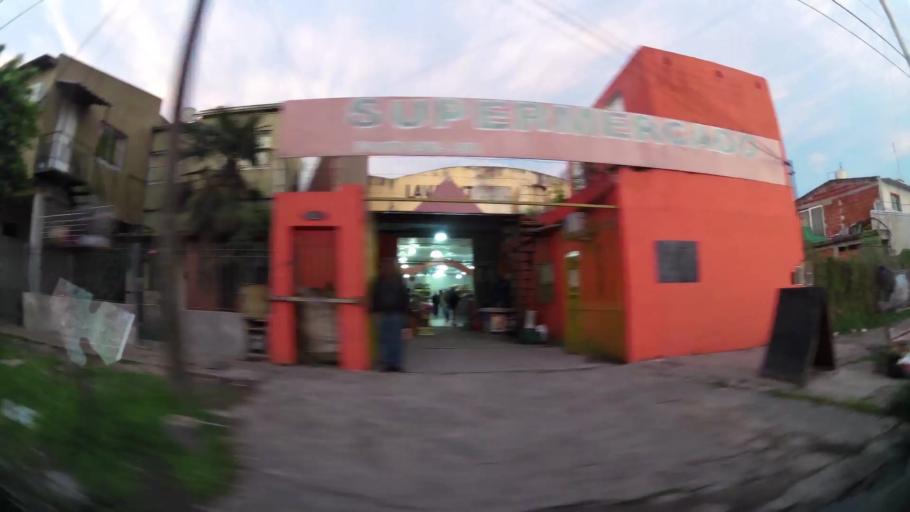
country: AR
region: Buenos Aires
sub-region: Partido de Lomas de Zamora
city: Lomas de Zamora
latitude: -34.7531
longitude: -58.3610
